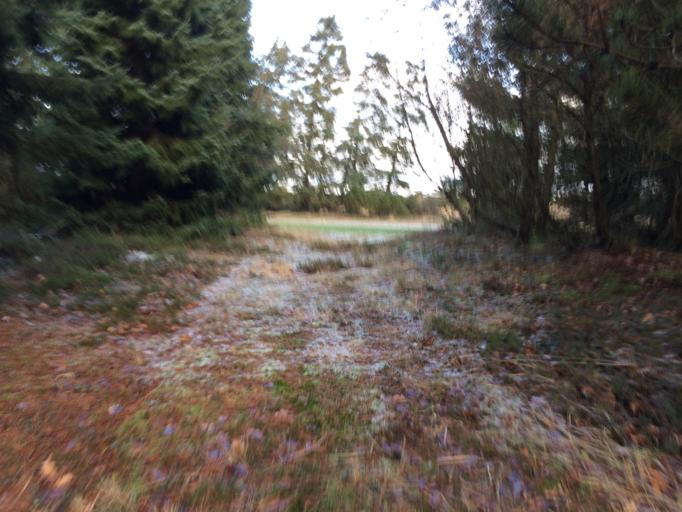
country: DK
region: Central Jutland
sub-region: Holstebro Kommune
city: Ulfborg
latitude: 56.2610
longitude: 8.3976
